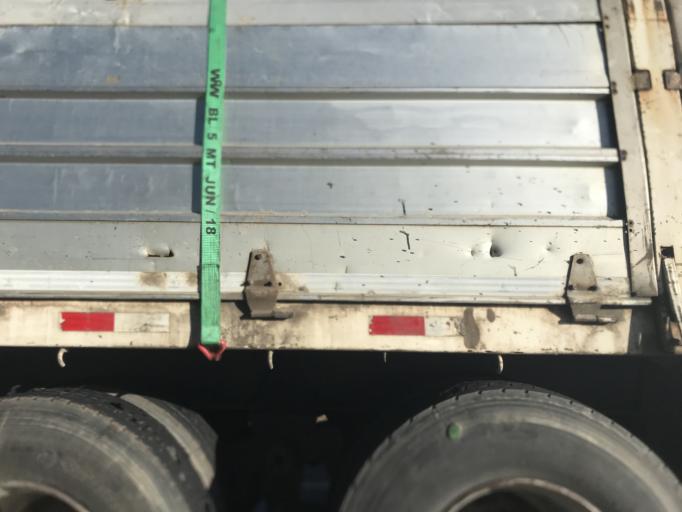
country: BO
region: La Paz
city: Tiahuanaco
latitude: -16.5649
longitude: -68.6377
